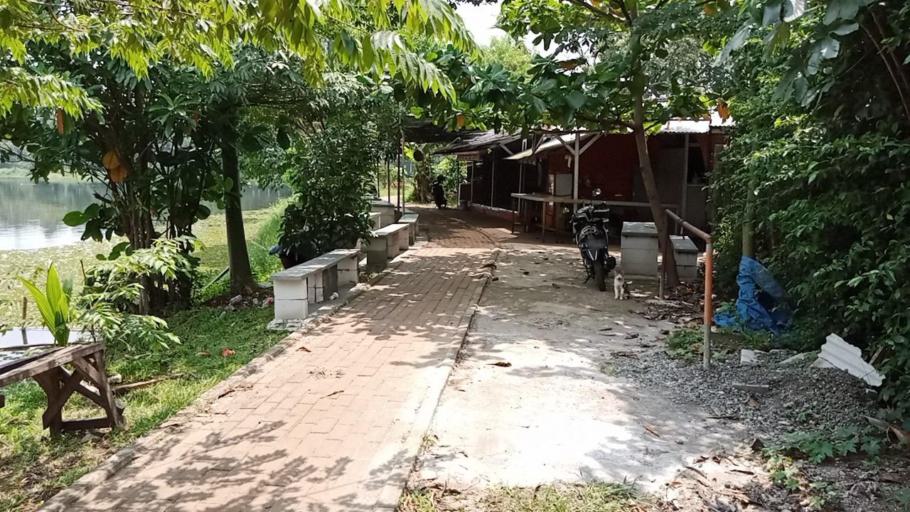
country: ID
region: West Java
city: Sawangan
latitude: -6.3867
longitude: 106.7571
